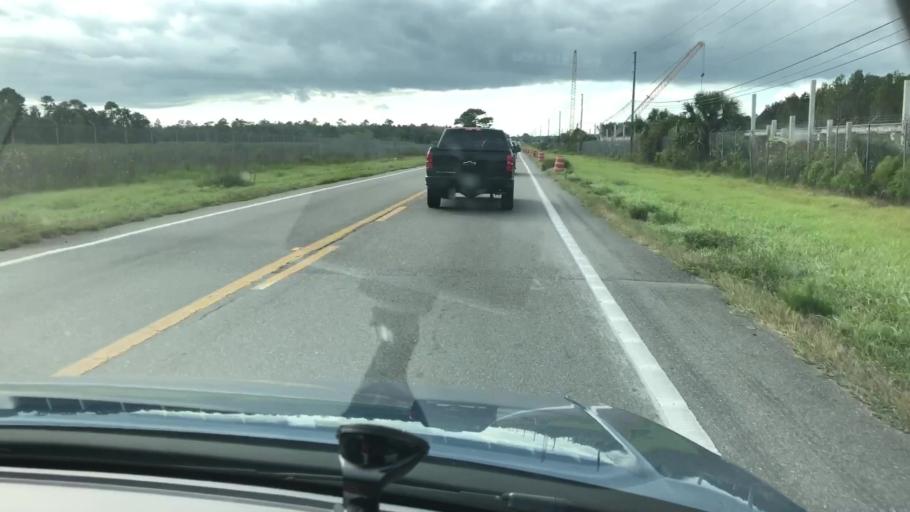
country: US
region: Florida
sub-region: Lake County
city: Mount Plymouth
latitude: 28.8107
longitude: -81.4458
